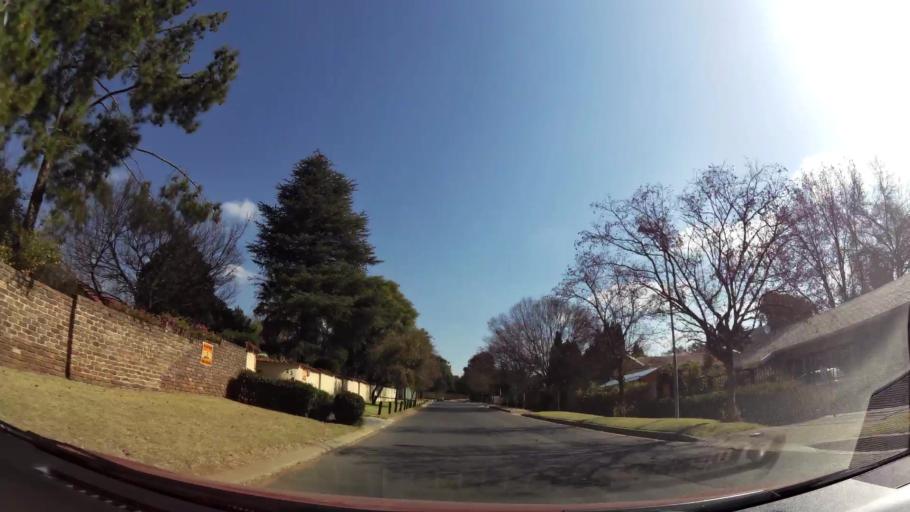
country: ZA
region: Gauteng
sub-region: City of Johannesburg Metropolitan Municipality
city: Roodepoort
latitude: -26.0785
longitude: 27.9401
